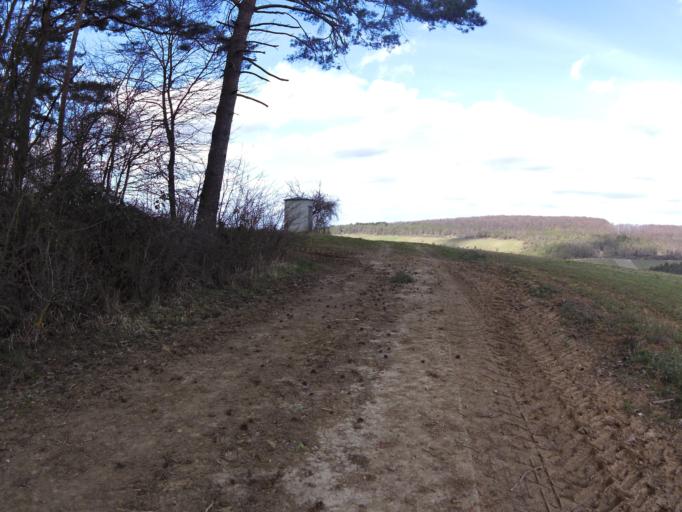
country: DE
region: Bavaria
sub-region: Regierungsbezirk Unterfranken
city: Erlabrunn
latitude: 49.8388
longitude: 9.8213
